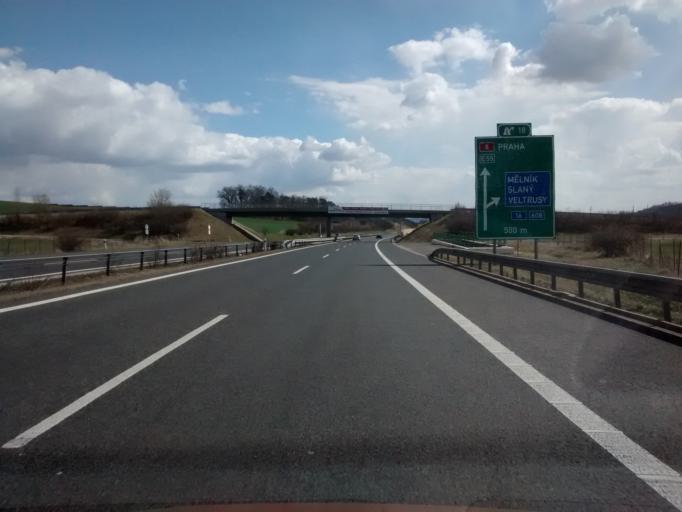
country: CZ
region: Central Bohemia
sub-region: Okres Melnik
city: Veltrusy
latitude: 50.3194
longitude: 14.3091
